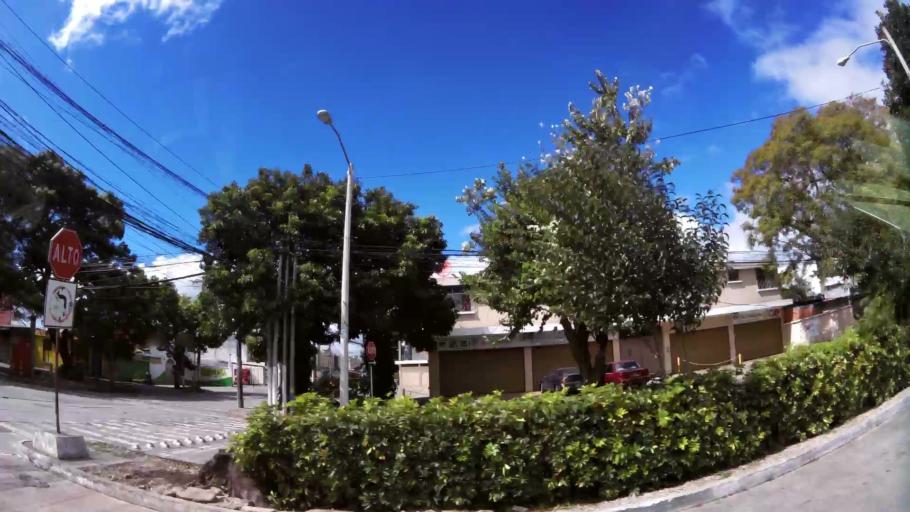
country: GT
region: Guatemala
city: Guatemala City
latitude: 14.6038
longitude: -90.5246
